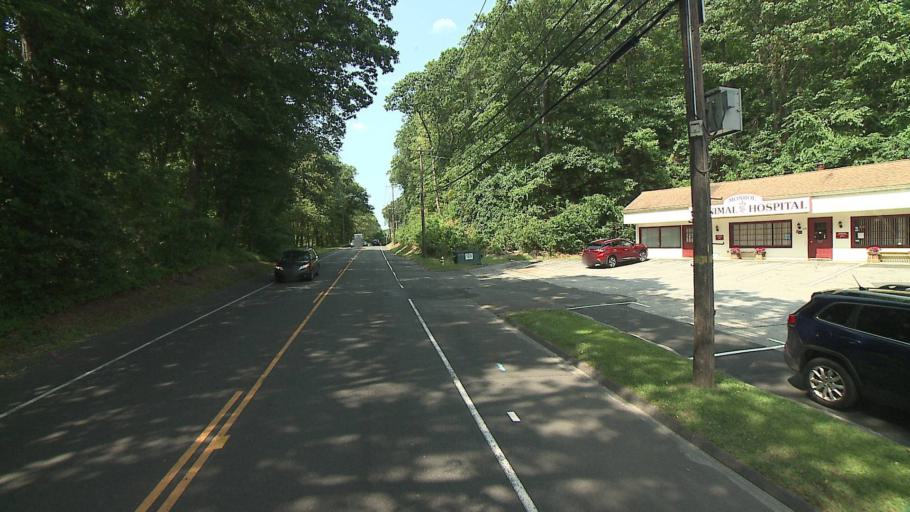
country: US
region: Connecticut
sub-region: Fairfield County
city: Trumbull
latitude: 41.3117
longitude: -73.2585
